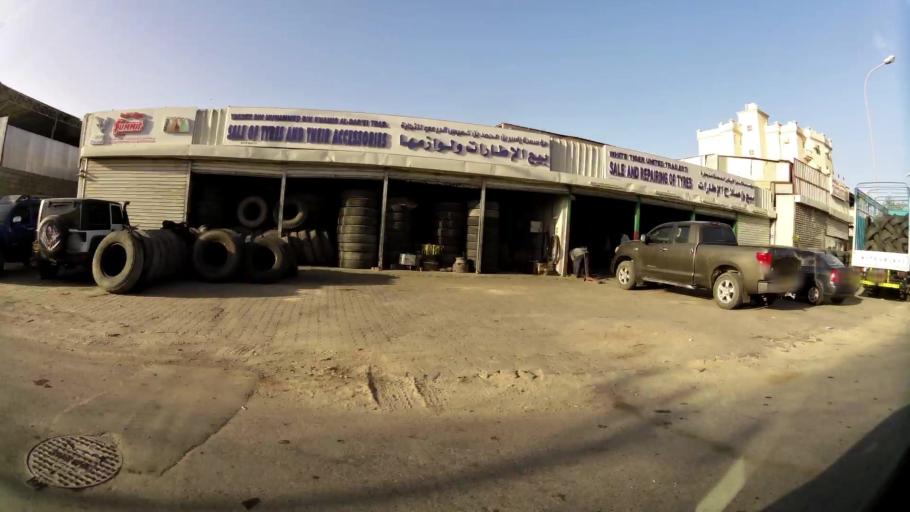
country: OM
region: Muhafazat Masqat
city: Muscat
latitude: 23.5859
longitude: 58.5554
